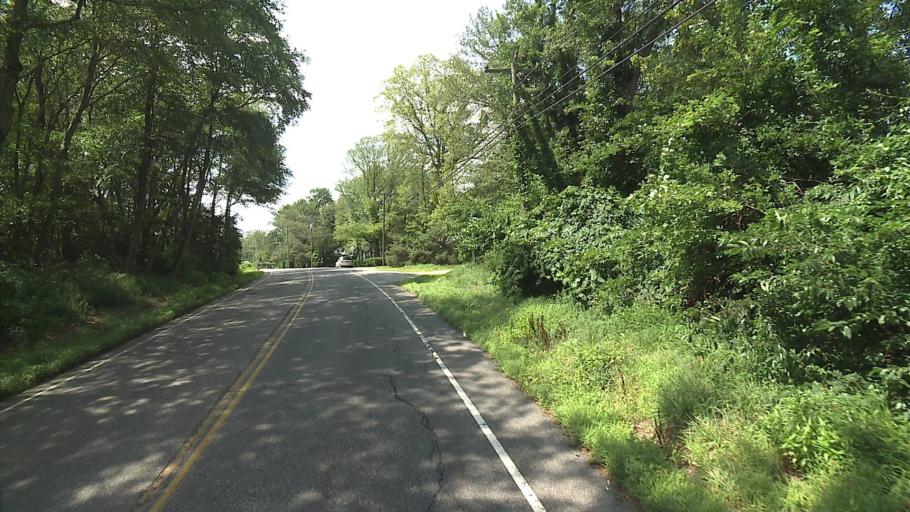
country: US
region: Connecticut
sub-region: New London County
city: Montville Center
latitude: 41.5047
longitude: -72.2386
